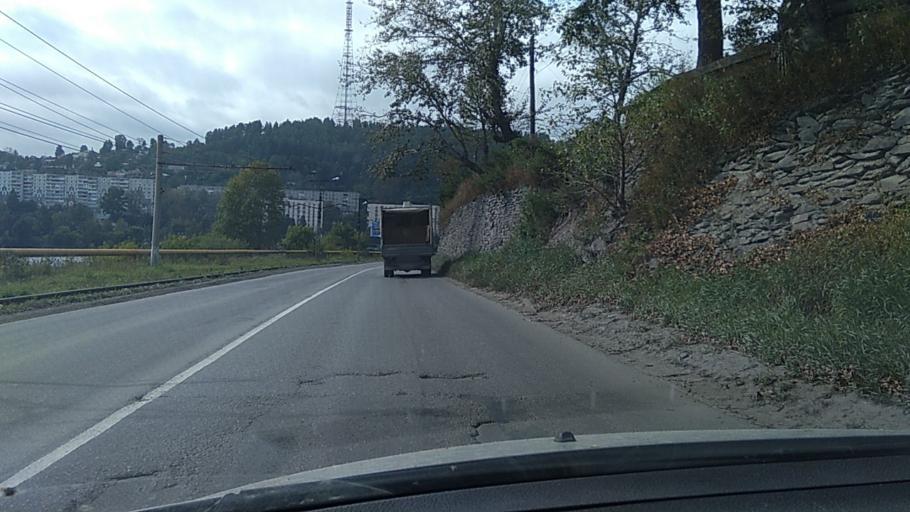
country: RU
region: Chelyabinsk
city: Zlatoust
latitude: 55.1726
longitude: 59.6807
